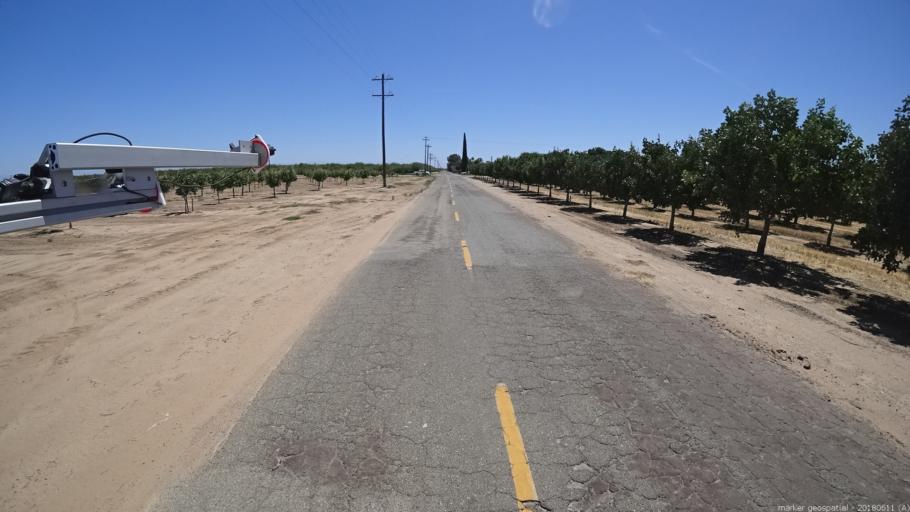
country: US
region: California
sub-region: Madera County
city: Fairmead
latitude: 37.0254
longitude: -120.1485
